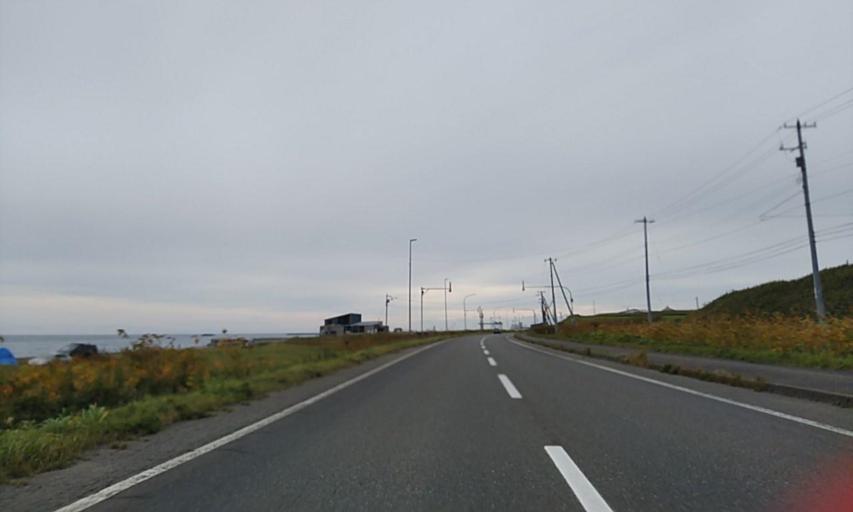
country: JP
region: Hokkaido
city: Makubetsu
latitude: 45.3484
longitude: 142.1520
